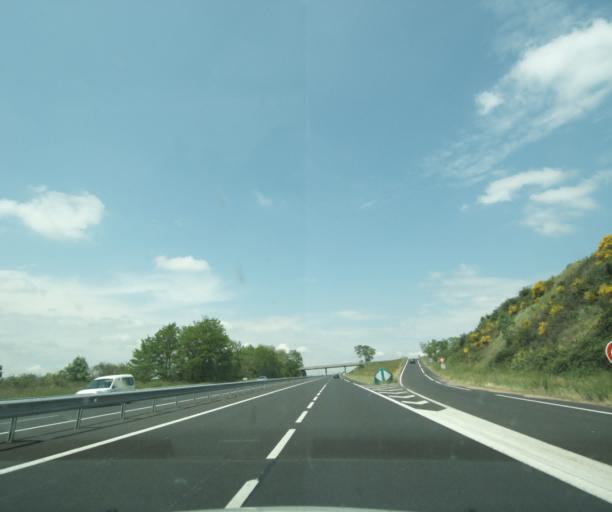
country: FR
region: Auvergne
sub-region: Departement de la Haute-Loire
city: Lempdes-sur-Allagnon
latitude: 45.4215
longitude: 3.2736
